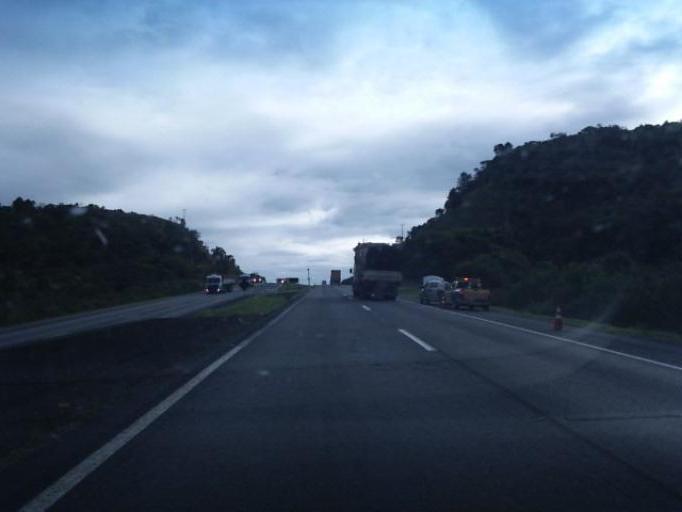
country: BR
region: Parana
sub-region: Campina Grande Do Sul
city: Campina Grande do Sul
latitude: -25.2688
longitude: -48.9182
